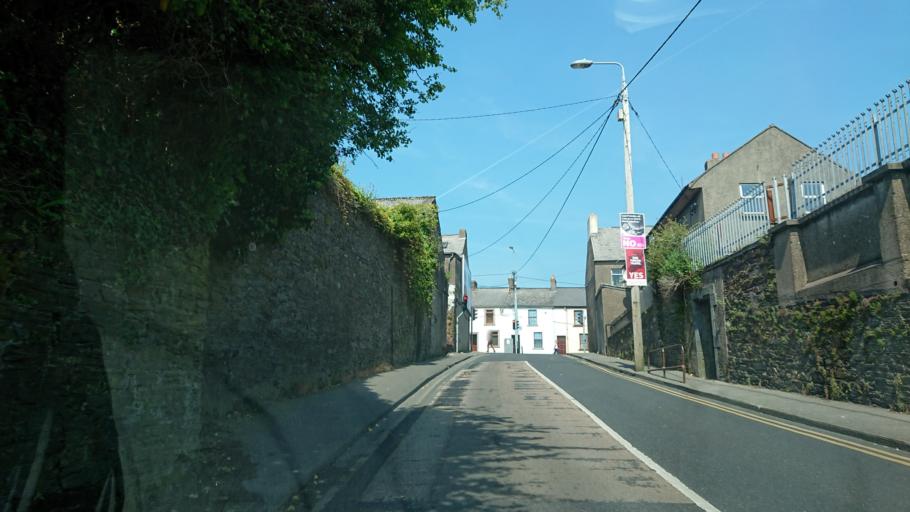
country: IE
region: Munster
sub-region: Waterford
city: Waterford
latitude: 52.2560
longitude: -7.1182
